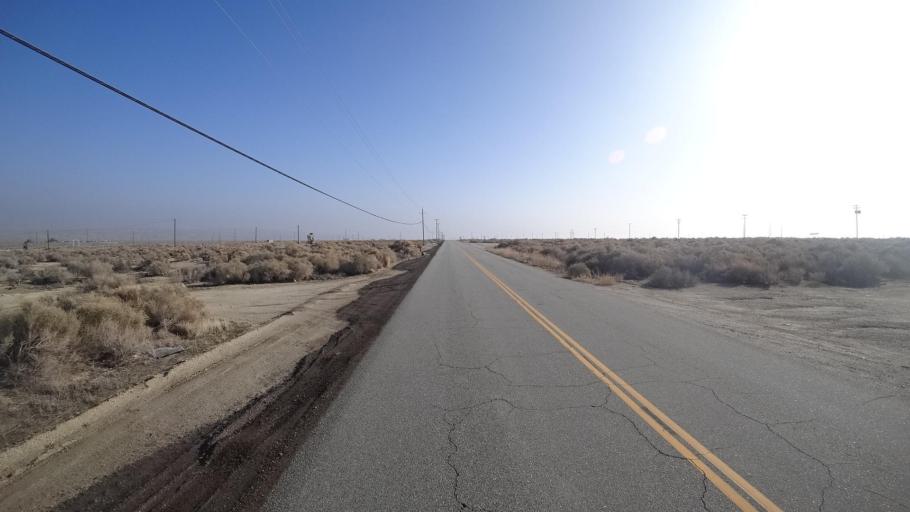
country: US
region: California
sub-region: Kern County
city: Taft Heights
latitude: 35.1801
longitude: -119.5354
